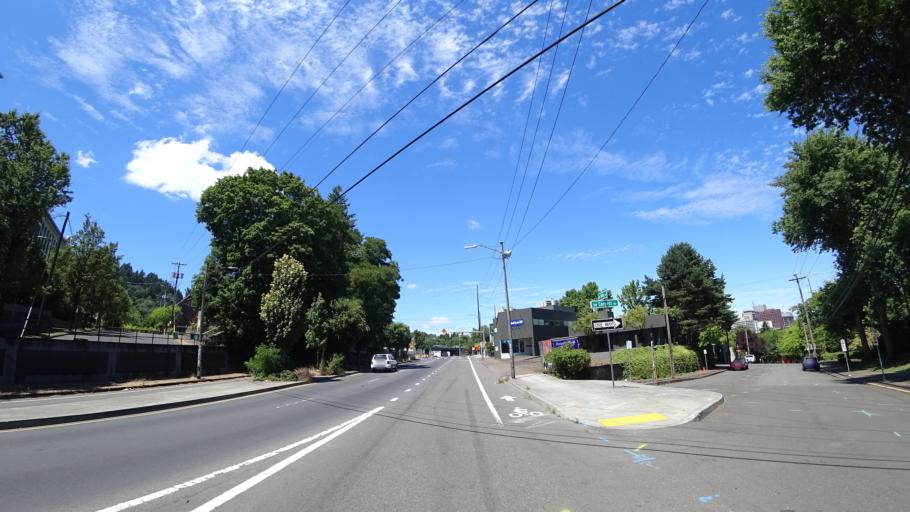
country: US
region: Oregon
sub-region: Multnomah County
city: Portland
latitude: 45.5022
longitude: -122.6754
